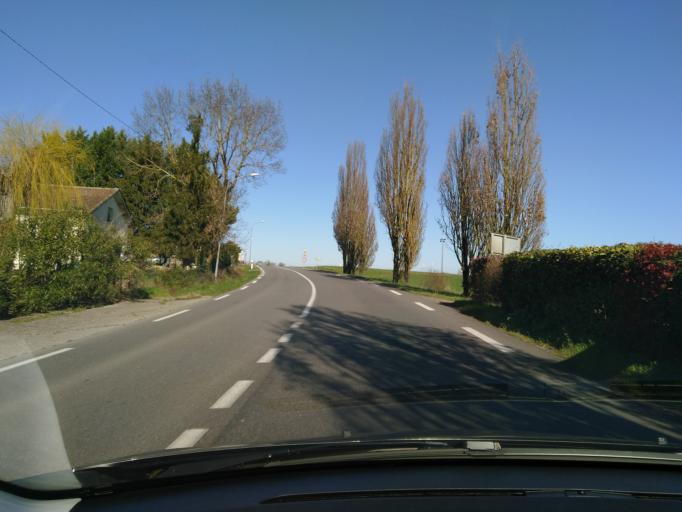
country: FR
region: Aquitaine
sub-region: Departement du Lot-et-Garonne
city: Cancon
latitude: 44.5435
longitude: 0.6250
